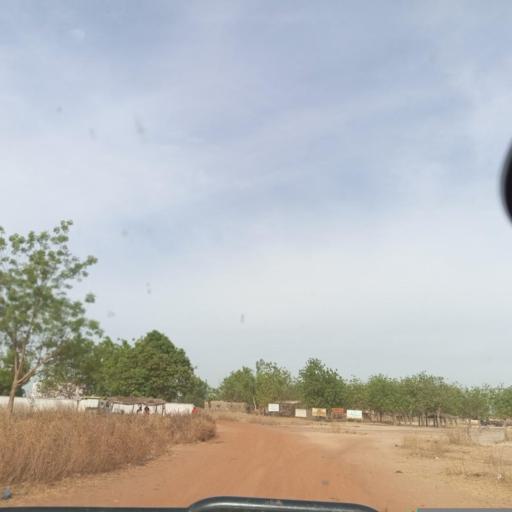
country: ML
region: Koulikoro
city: Koulikoro
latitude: 13.1113
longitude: -7.6525
